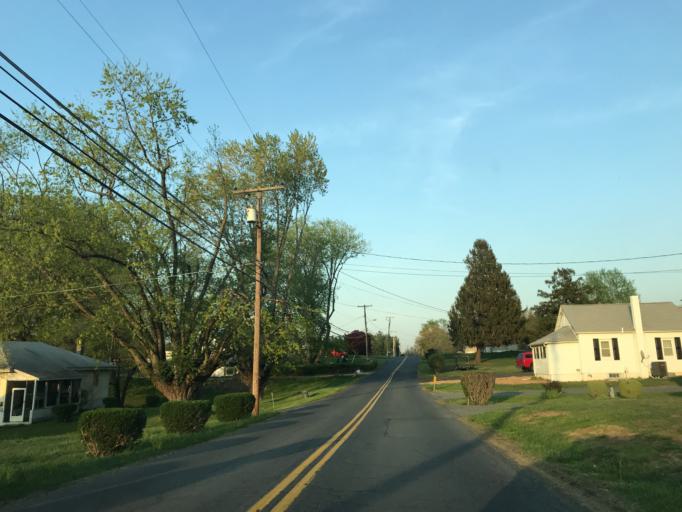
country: US
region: Maryland
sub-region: Harford County
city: Jarrettsville
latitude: 39.5923
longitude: -76.4317
